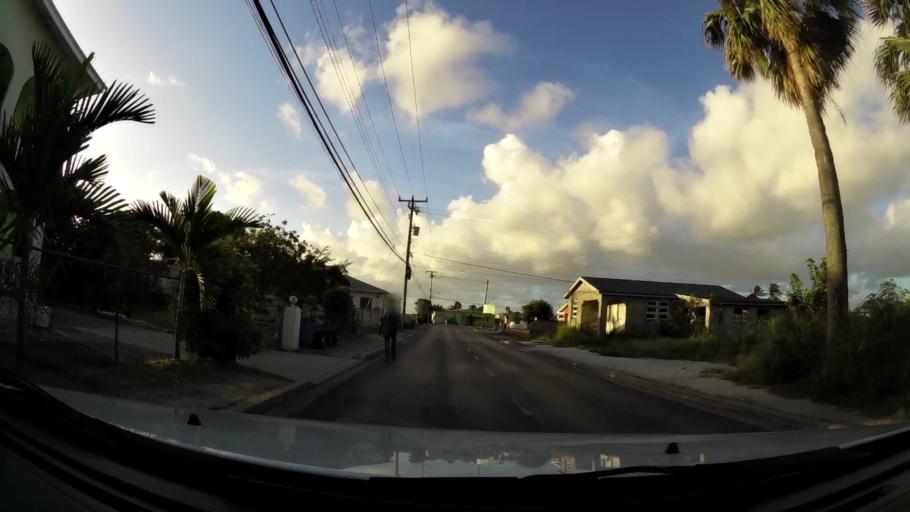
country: BB
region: Saint Philip
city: Crane
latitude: 13.0938
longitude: -59.4658
